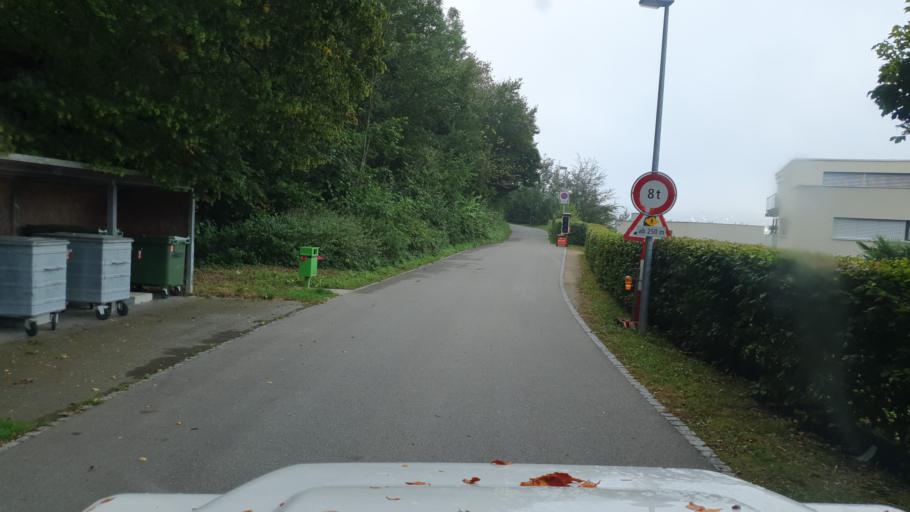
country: CH
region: Aargau
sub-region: Bezirk Baden
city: Mellingen
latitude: 47.4258
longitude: 8.2728
